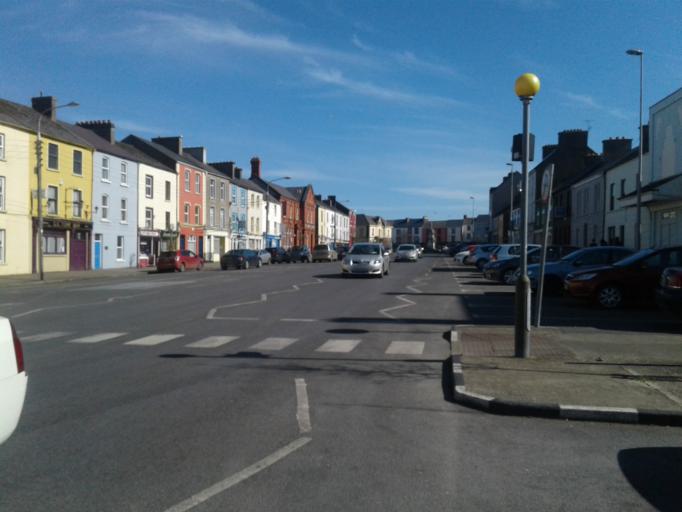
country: IE
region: Munster
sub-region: An Clar
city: Kilrush
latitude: 52.6371
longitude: -9.4866
